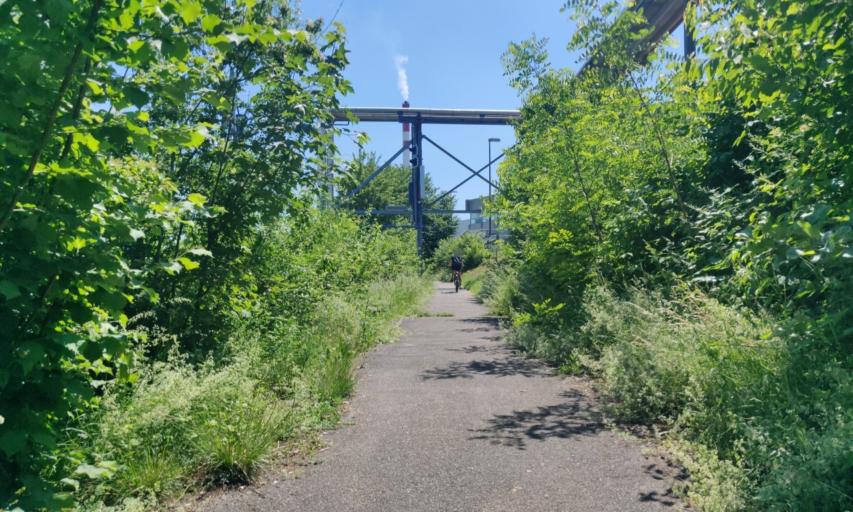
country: DE
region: Baden-Wuerttemberg
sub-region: Freiburg Region
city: Grenzach-Wyhlen
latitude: 47.5384
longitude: 7.6631
